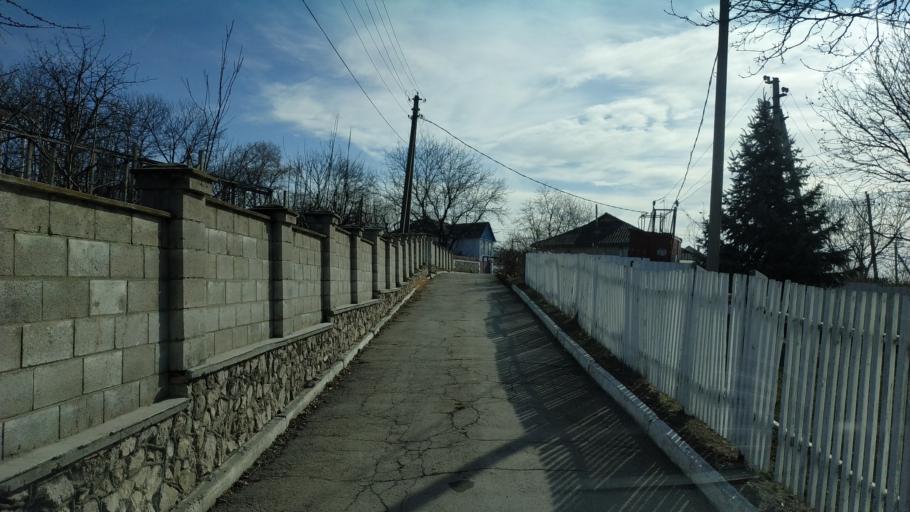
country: MD
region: Chisinau
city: Vatra
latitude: 47.0280
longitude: 28.6336
